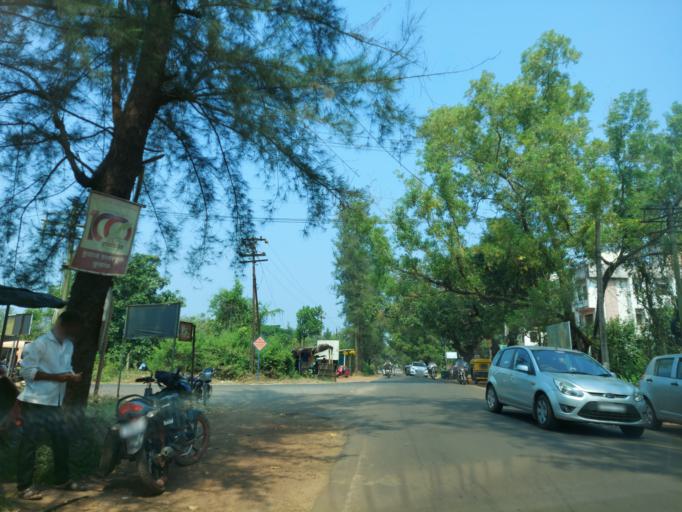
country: IN
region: Maharashtra
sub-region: Sindhudurg
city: Kudal
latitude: 15.9975
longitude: 73.6853
